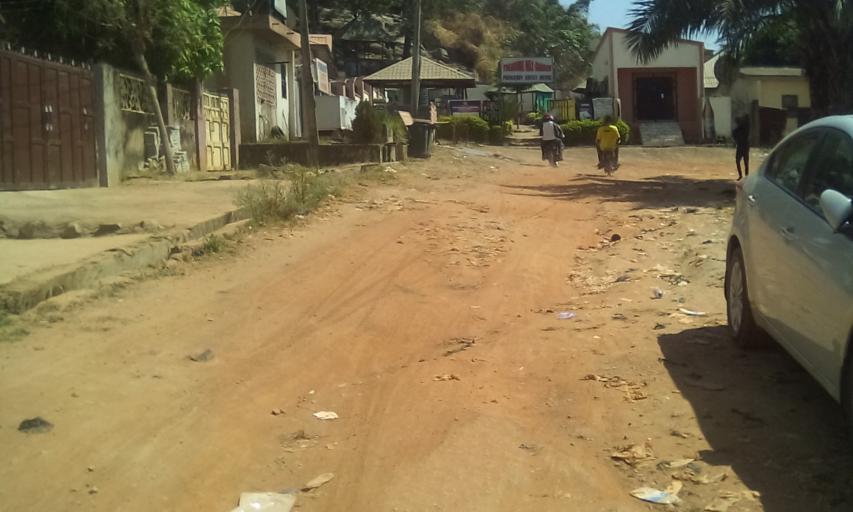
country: NG
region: Abuja Federal Capital Territory
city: Abuja
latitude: 8.9854
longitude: 7.3707
